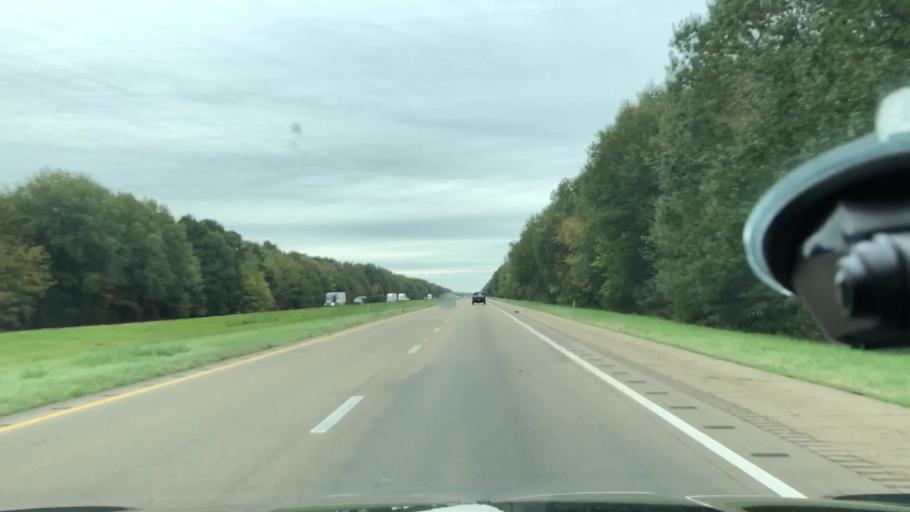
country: US
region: Texas
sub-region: Morris County
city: Naples
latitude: 33.3245
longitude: -94.6809
